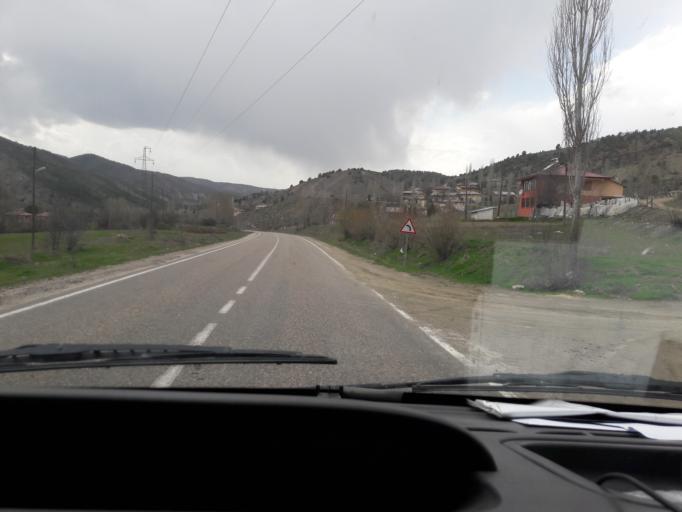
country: TR
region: Giresun
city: Alucra
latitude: 40.2749
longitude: 38.8448
